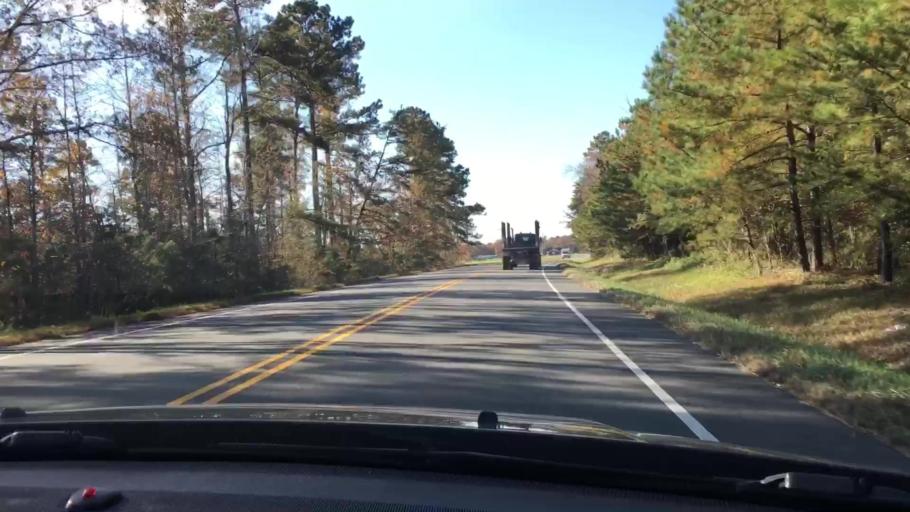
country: US
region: Virginia
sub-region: Hanover County
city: Hanover
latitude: 37.8116
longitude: -77.2906
